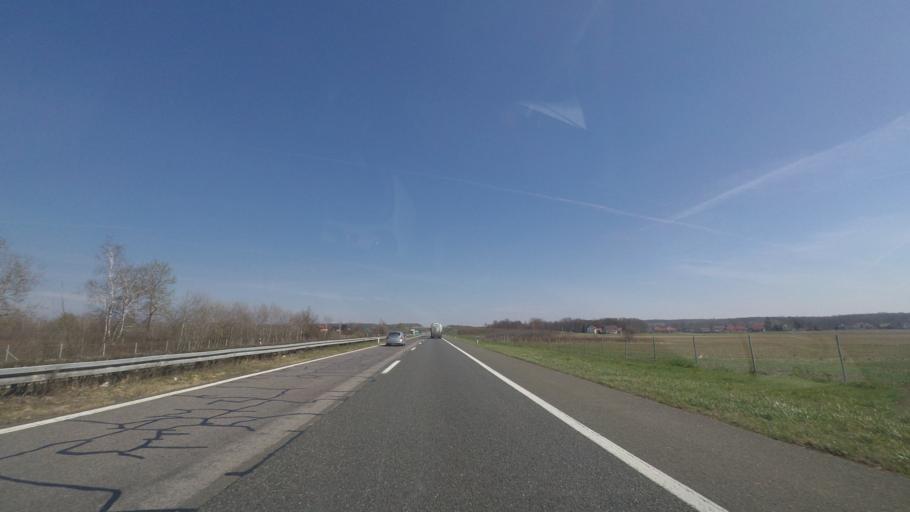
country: HR
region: Grad Zagreb
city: Horvati
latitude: 45.6794
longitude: 15.7687
